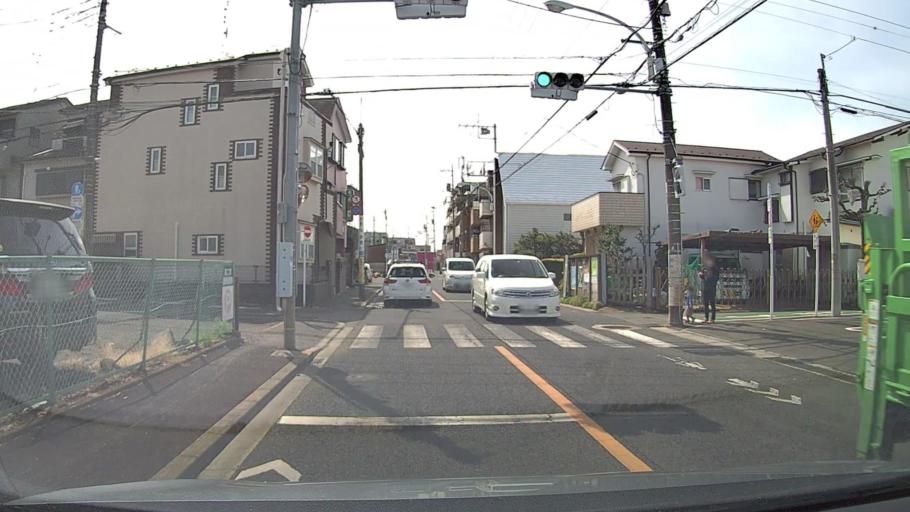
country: JP
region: Tokyo
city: Nishi-Tokyo-shi
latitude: 35.7403
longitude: 139.5526
